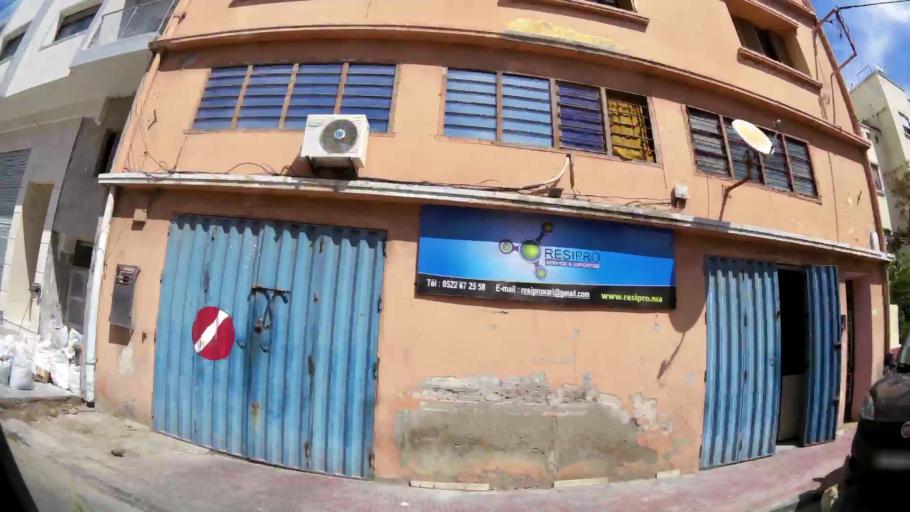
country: MA
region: Grand Casablanca
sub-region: Mediouna
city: Tit Mellil
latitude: 33.6097
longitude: -7.5322
